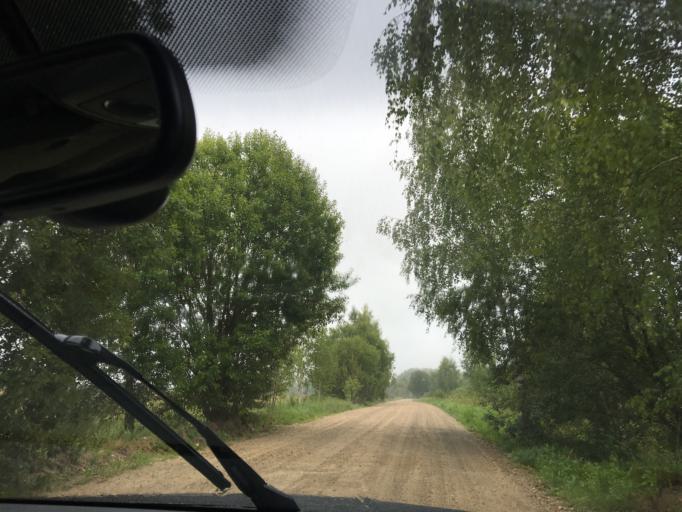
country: RU
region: Kaluga
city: Borovsk
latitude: 55.1693
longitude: 36.4575
